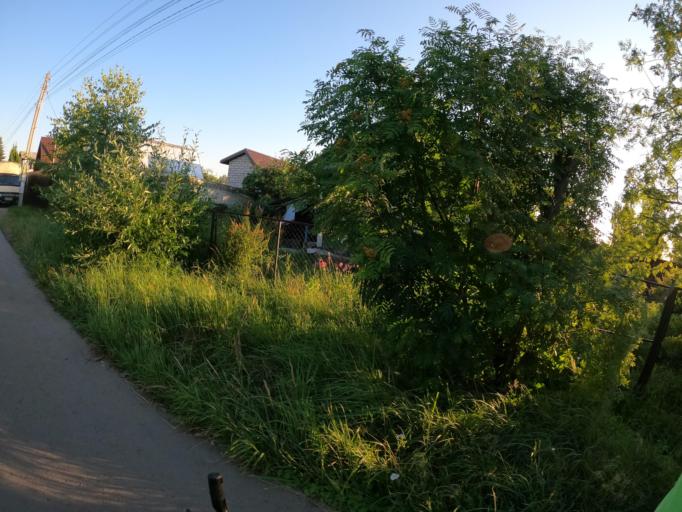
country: RU
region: Moskovskaya
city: Beloozerskiy
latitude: 55.4690
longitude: 38.4185
